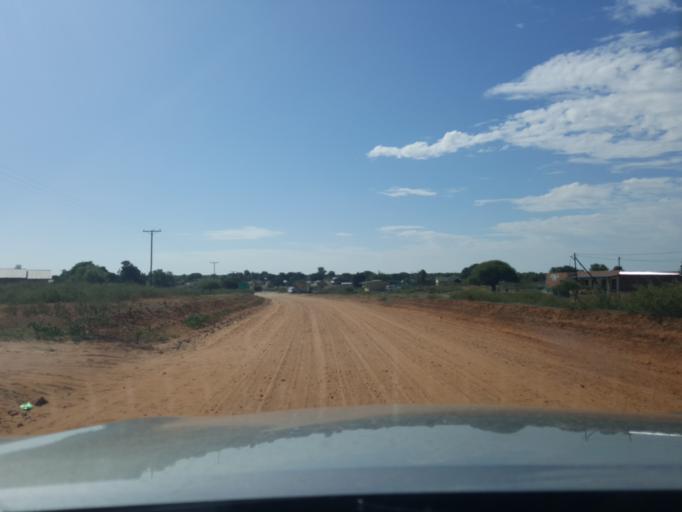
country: BW
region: Kweneng
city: Khudumelapye
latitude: -23.6985
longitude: 24.7197
